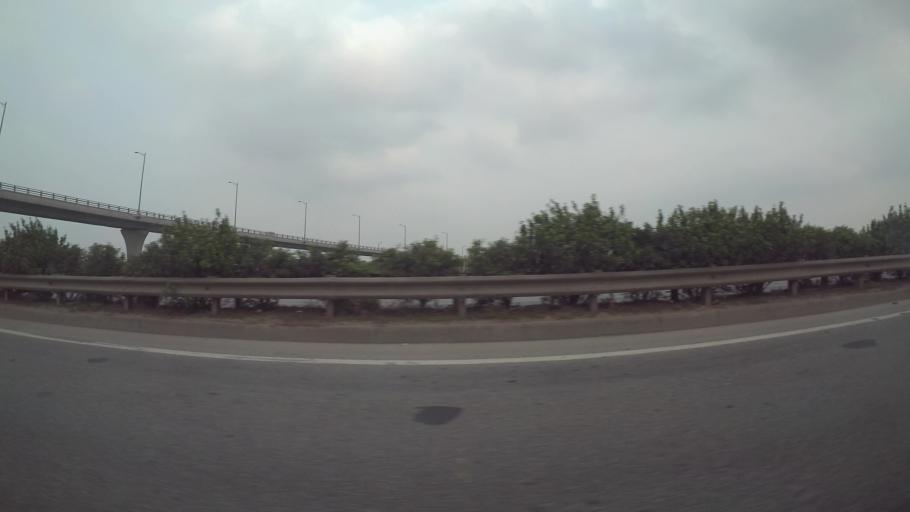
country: VN
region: Ha Noi
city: Trau Quy
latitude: 21.0129
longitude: 105.9183
